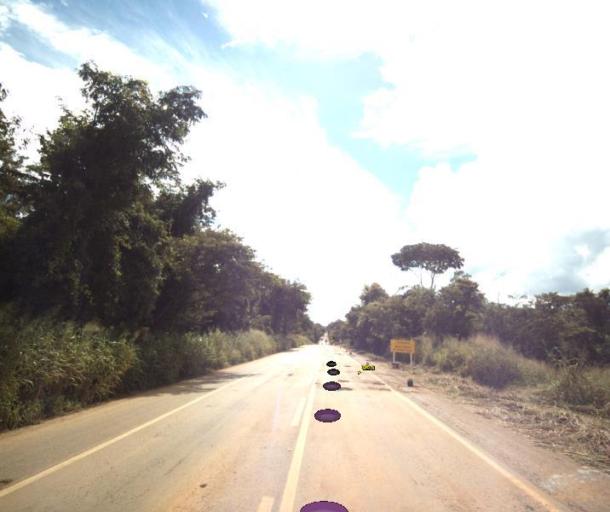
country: BR
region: Goias
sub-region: Petrolina De Goias
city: Petrolina de Goias
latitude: -16.0083
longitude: -49.1276
